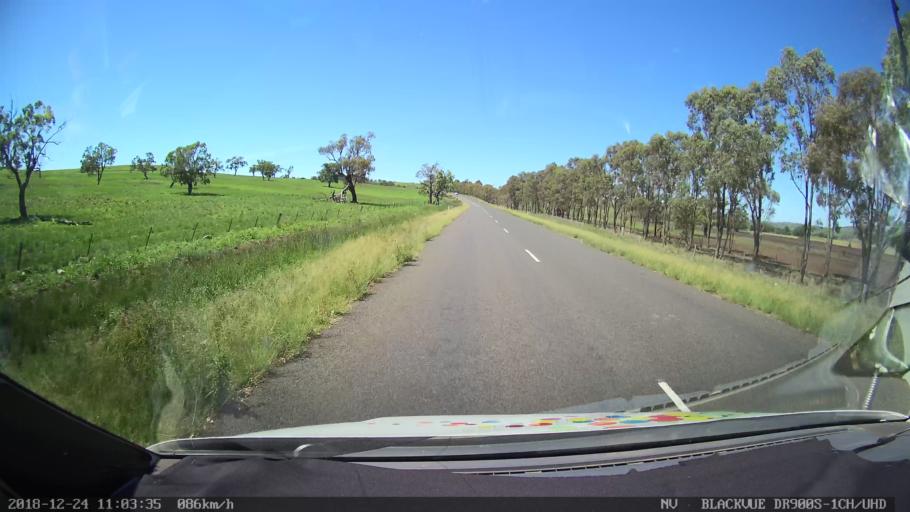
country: AU
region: New South Wales
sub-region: Upper Hunter Shire
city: Merriwa
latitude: -32.0986
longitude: 150.3688
